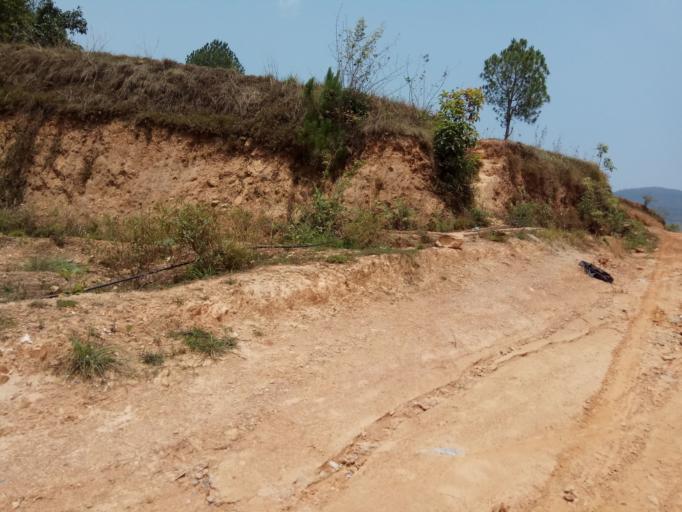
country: NP
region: Central Region
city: Kirtipur
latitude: 27.8910
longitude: 85.0822
